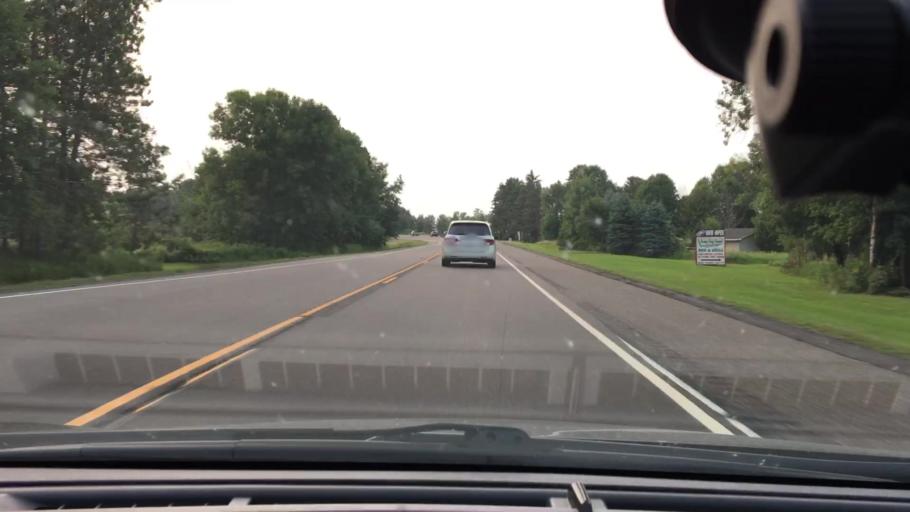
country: US
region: Minnesota
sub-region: Mille Lacs County
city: Vineland
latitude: 46.1324
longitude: -93.6896
